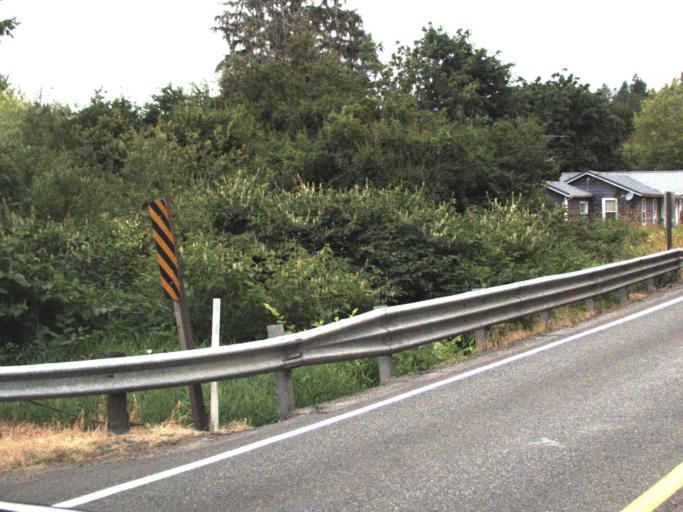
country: US
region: Washington
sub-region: King County
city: Lake Marcel-Stillwater
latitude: 47.6781
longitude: -121.9074
